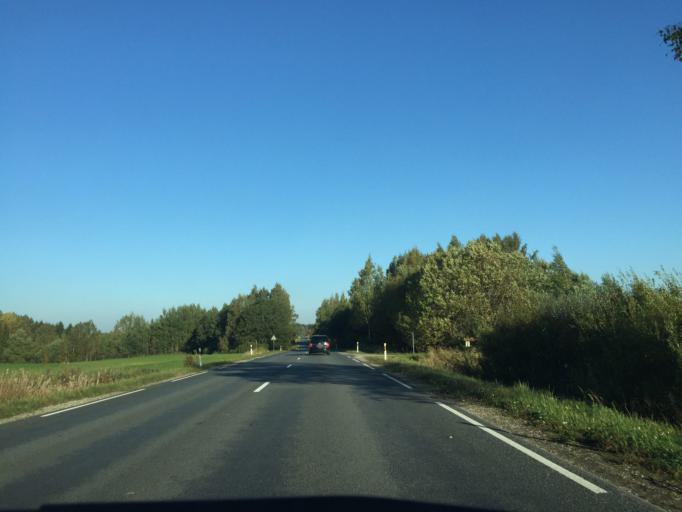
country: LV
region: Raunas
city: Rauna
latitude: 57.2458
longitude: 25.5538
